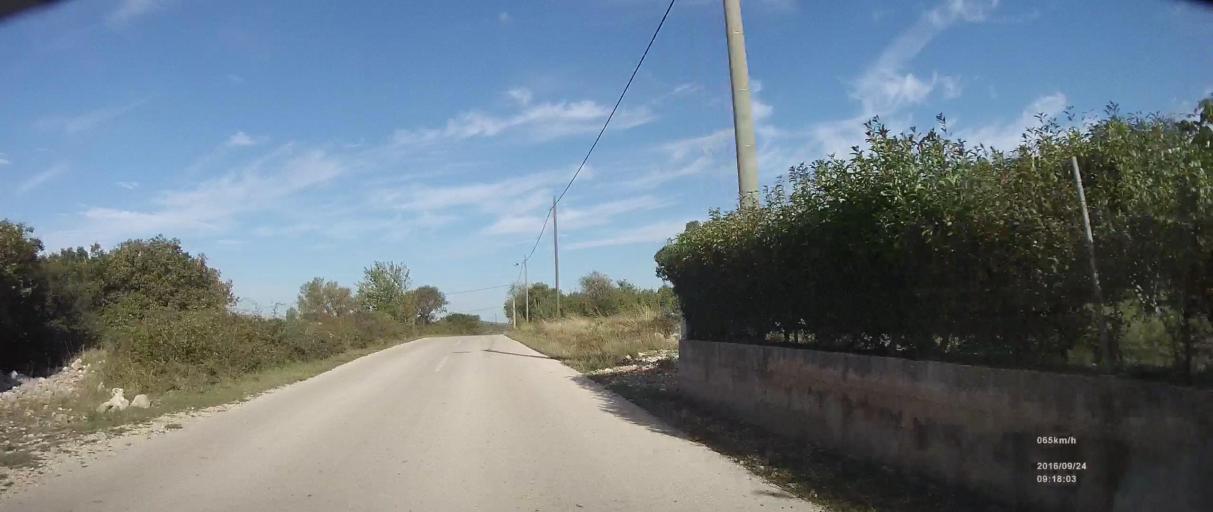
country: HR
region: Zadarska
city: Polaca
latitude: 44.0543
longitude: 15.5155
